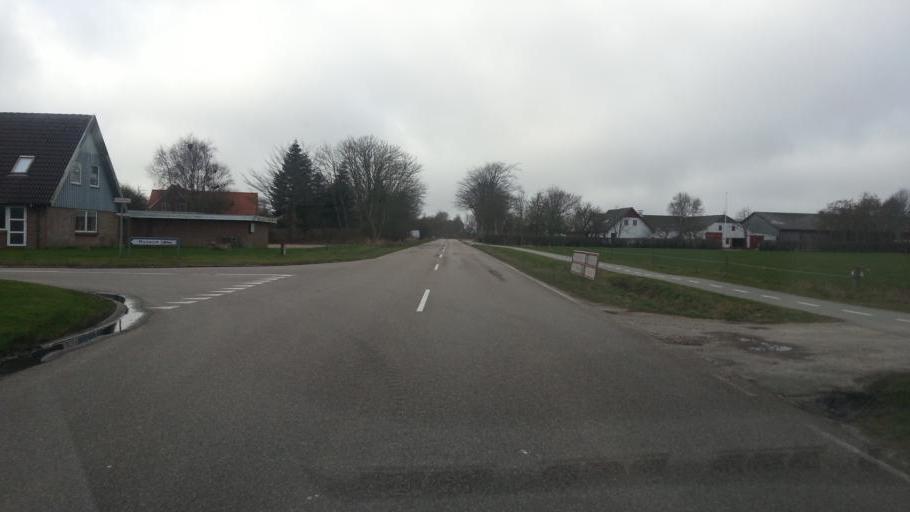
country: DK
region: South Denmark
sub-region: Varde Kommune
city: Oksbol
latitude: 55.6219
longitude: 8.2970
